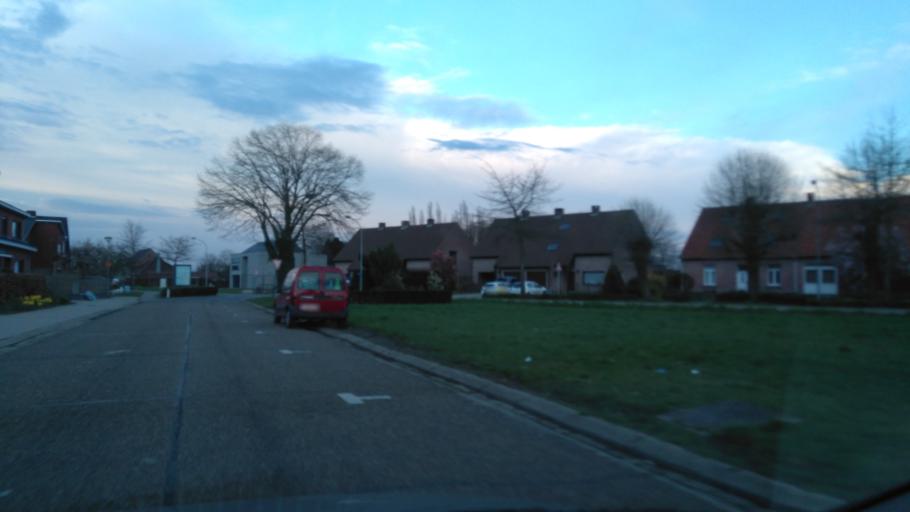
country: BE
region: Flanders
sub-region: Provincie Antwerpen
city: Turnhout
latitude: 51.3050
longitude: 4.9628
